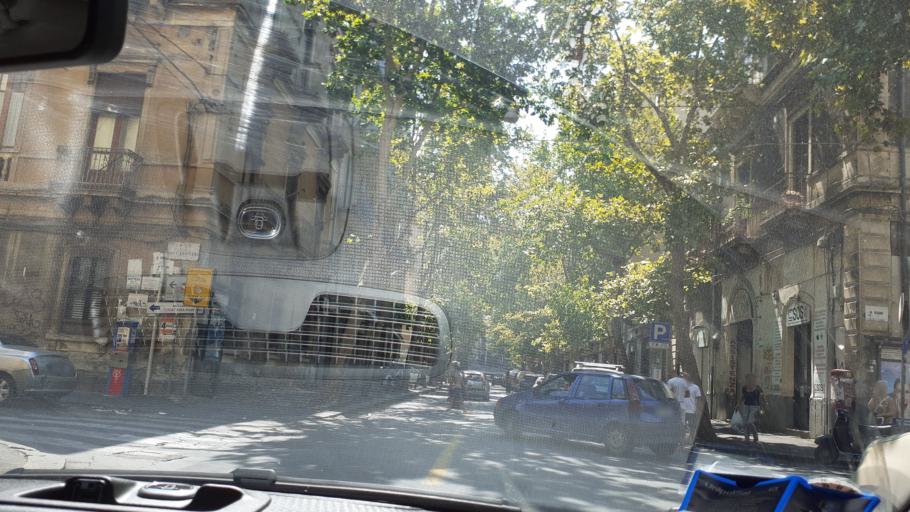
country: IT
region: Sicily
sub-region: Catania
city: Catania
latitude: 37.5089
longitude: 15.0792
